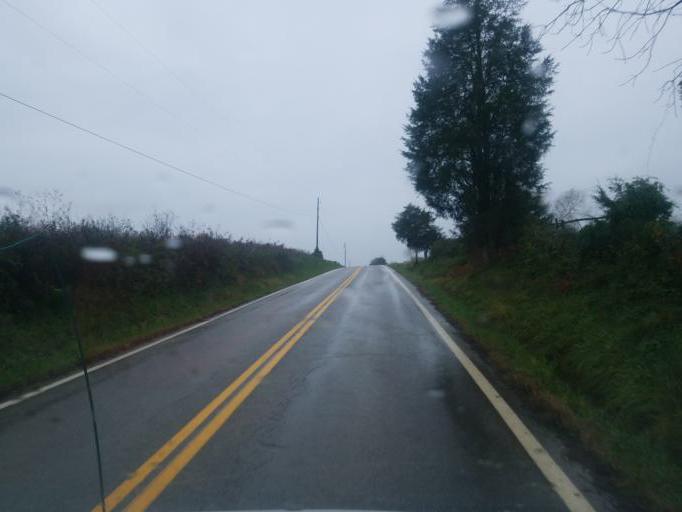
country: US
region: Ohio
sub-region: Washington County
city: Beverly
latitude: 39.4719
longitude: -81.7177
